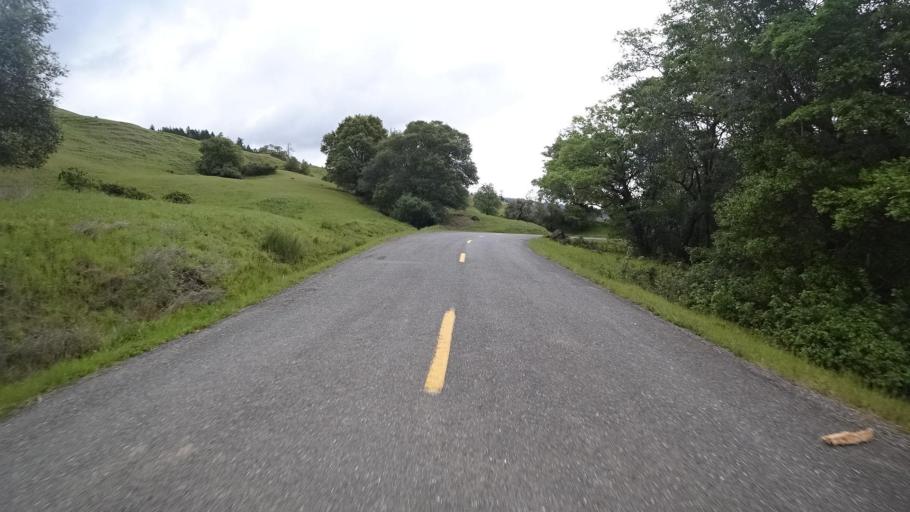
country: US
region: California
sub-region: Humboldt County
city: Redway
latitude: 40.2275
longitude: -123.6104
